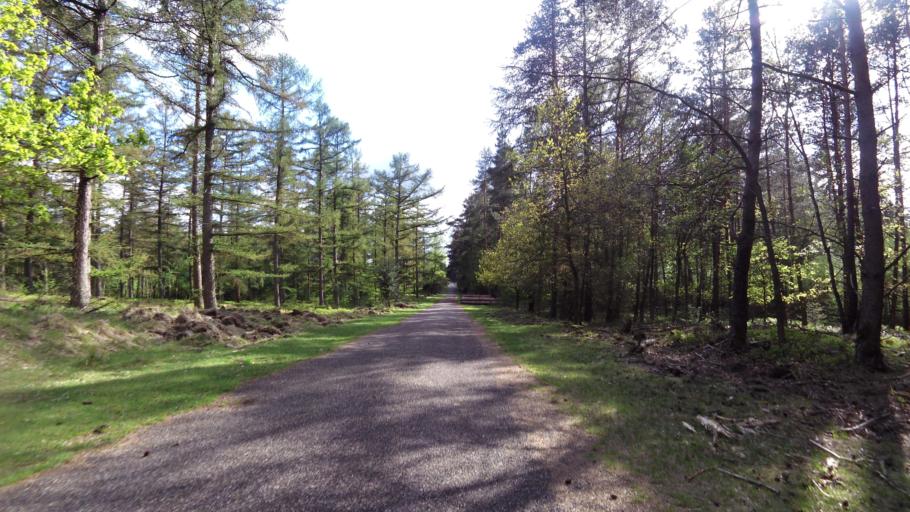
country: NL
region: Gelderland
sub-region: Gemeente Apeldoorn
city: Loenen
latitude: 52.0955
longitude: 5.9744
